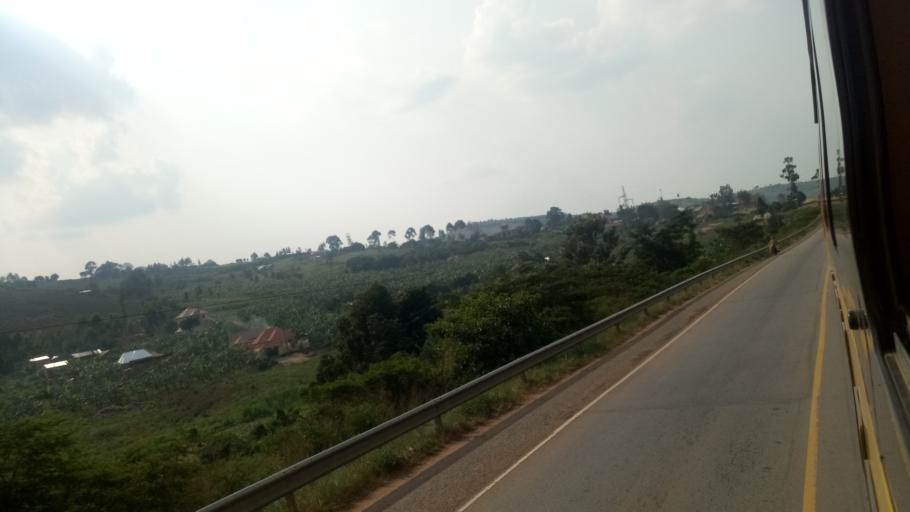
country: UG
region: Western Region
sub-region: Mbarara District
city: Mbarara
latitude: -0.5360
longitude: 30.7154
